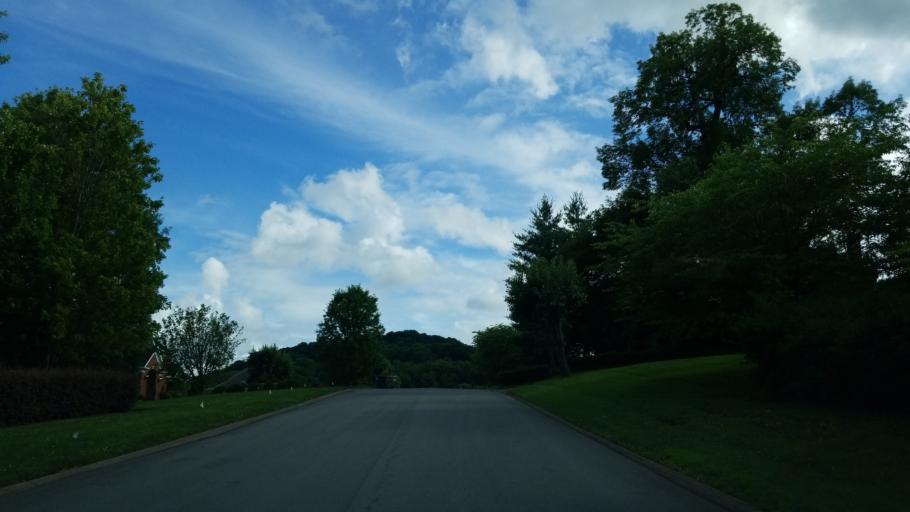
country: US
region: Tennessee
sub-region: Davidson County
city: Forest Hills
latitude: 36.0327
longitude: -86.8370
